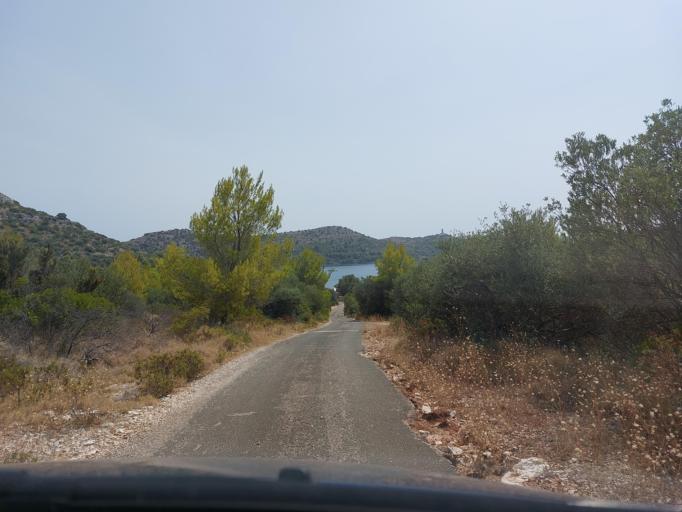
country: HR
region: Dubrovacko-Neretvanska
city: Smokvica
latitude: 42.7390
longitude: 16.8875
